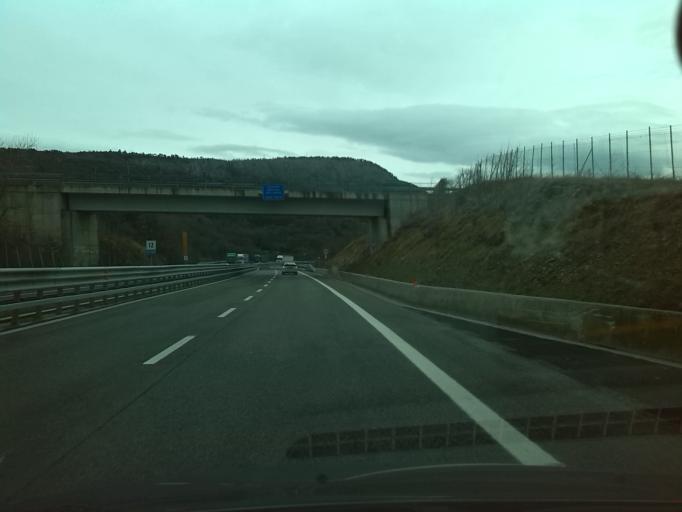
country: IT
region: Friuli Venezia Giulia
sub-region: Provincia di Trieste
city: Domio
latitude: 45.6297
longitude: 13.8249
